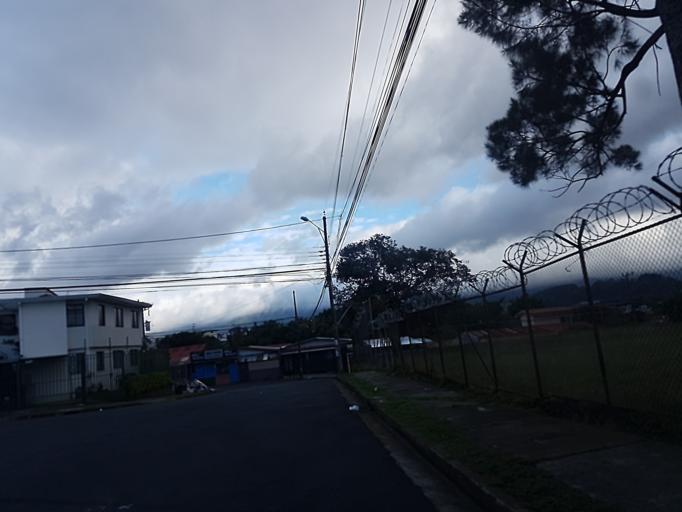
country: CR
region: San Jose
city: San Pedro
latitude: 9.9262
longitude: -84.0473
